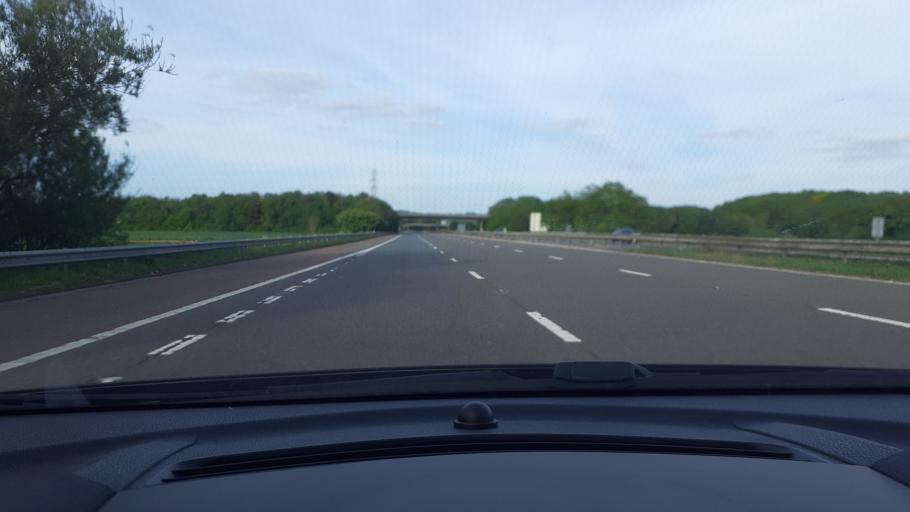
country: GB
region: England
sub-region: Lancashire
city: Skelmersdale
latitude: 53.5394
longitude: -2.8178
